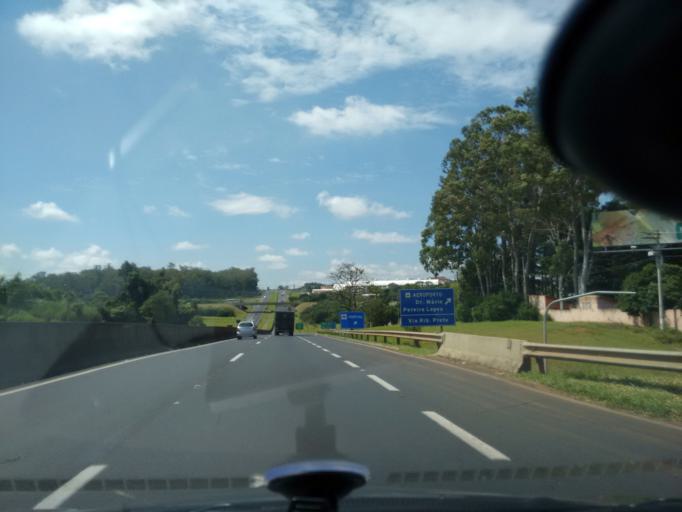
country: BR
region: Sao Paulo
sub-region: Sao Carlos
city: Sao Carlos
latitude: -21.9888
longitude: -47.8932
